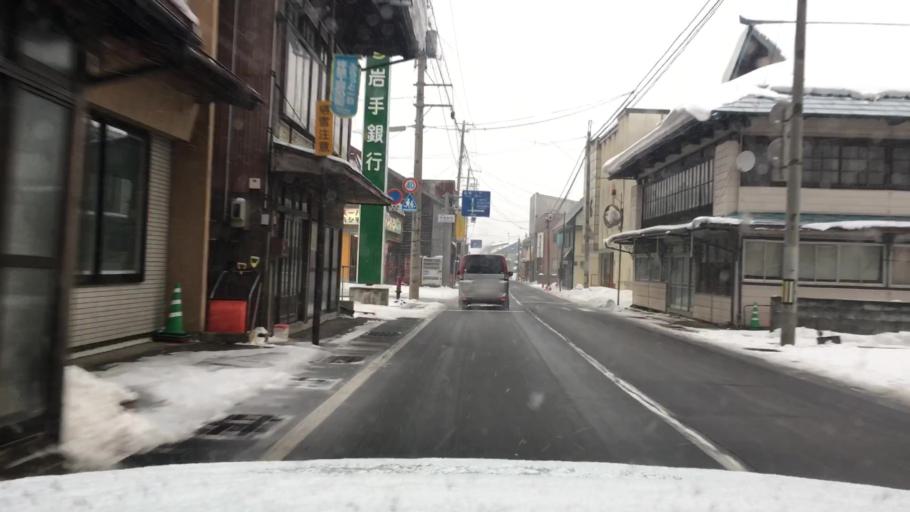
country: JP
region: Iwate
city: Ichinohe
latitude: 40.0984
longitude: 141.0477
